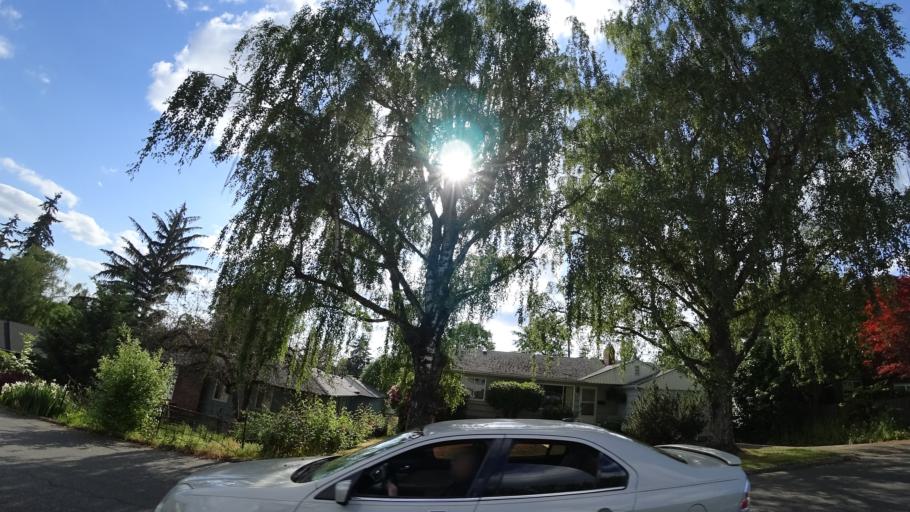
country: US
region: Oregon
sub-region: Washington County
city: Garden Home-Whitford
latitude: 45.4789
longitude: -122.7232
